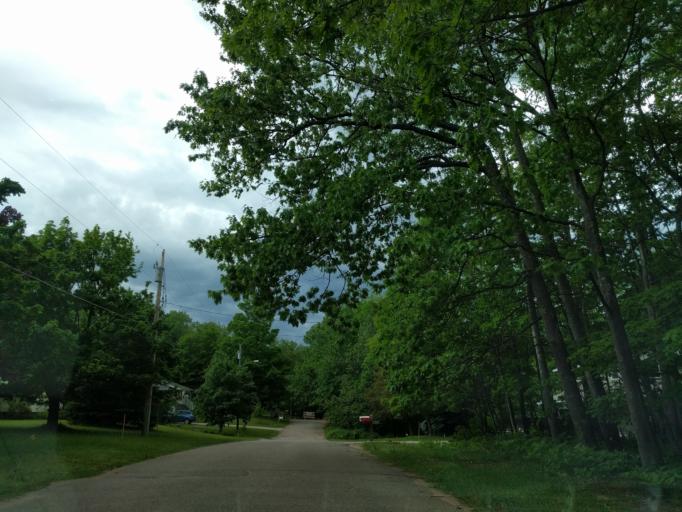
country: US
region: Michigan
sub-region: Marquette County
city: Trowbridge Park
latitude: 46.5571
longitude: -87.4462
